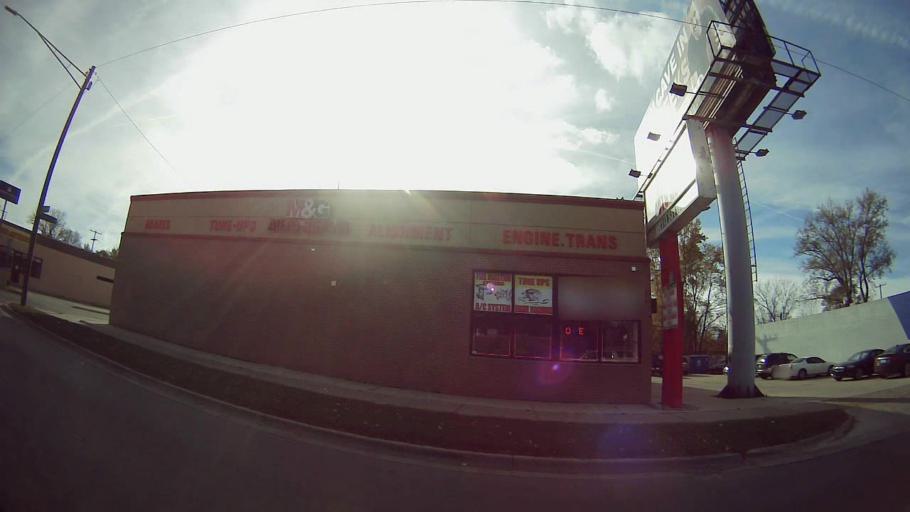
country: US
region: Michigan
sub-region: Oakland County
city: Southfield
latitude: 42.4440
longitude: -83.2264
